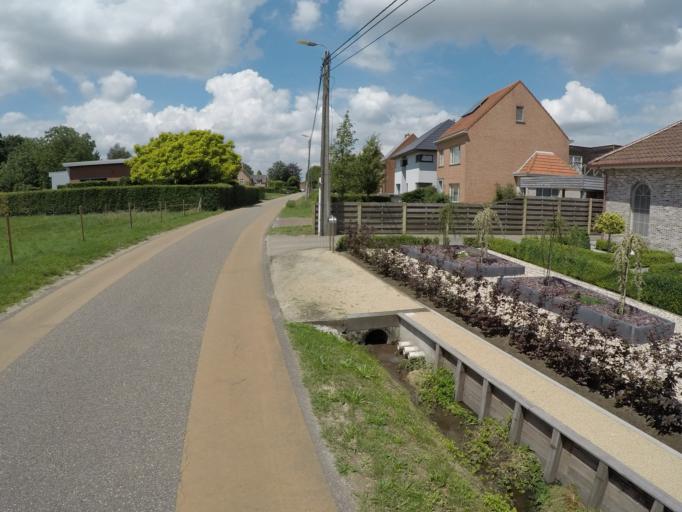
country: BE
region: Flanders
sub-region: Provincie Antwerpen
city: Lille
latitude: 51.2717
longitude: 4.8557
